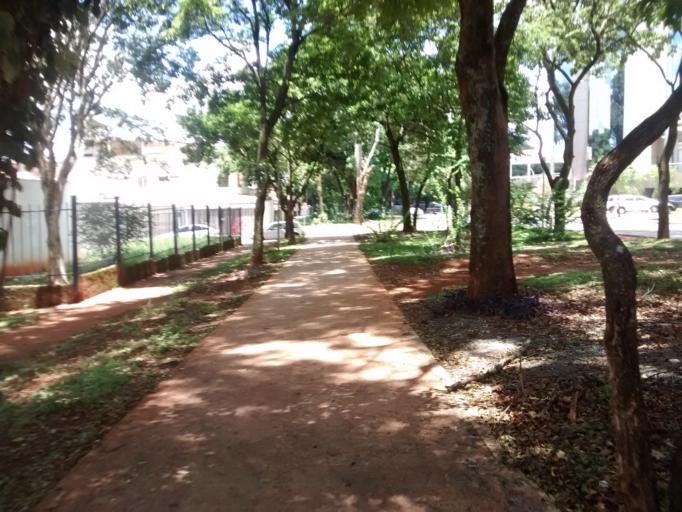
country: BR
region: Federal District
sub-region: Brasilia
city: Brasilia
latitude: -15.8138
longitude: -47.9126
